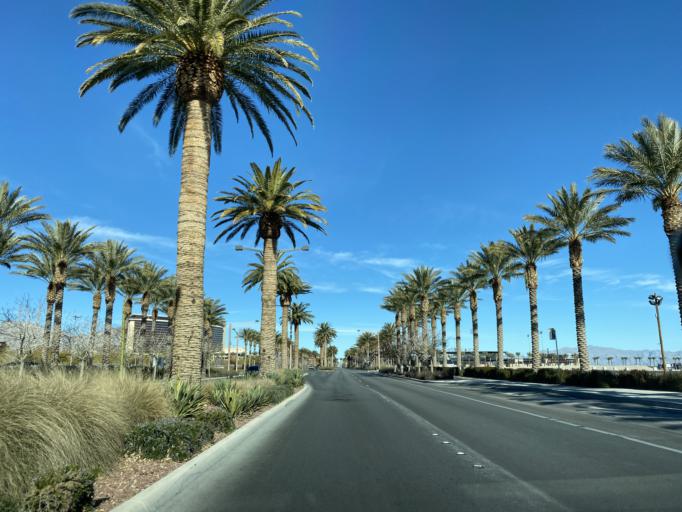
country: US
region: Nevada
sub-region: Clark County
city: Summerlin South
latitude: 36.1486
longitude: -115.3306
